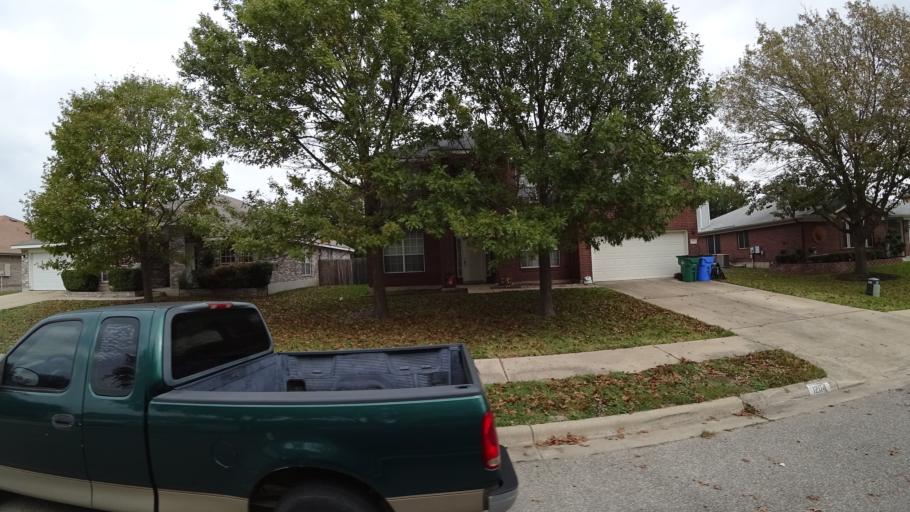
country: US
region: Texas
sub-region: Travis County
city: Pflugerville
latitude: 30.4391
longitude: -97.6075
